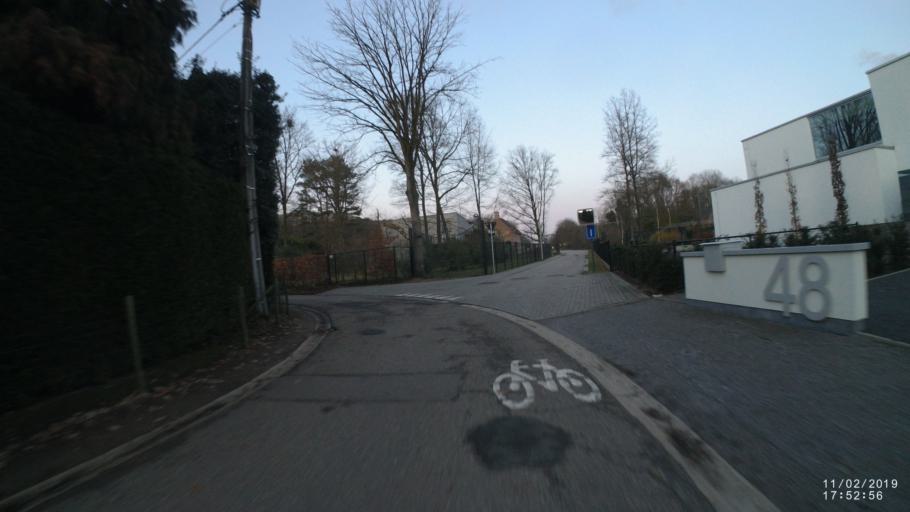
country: BE
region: Flanders
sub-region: Provincie Vlaams-Brabant
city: Rotselaar
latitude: 50.9600
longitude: 4.7525
